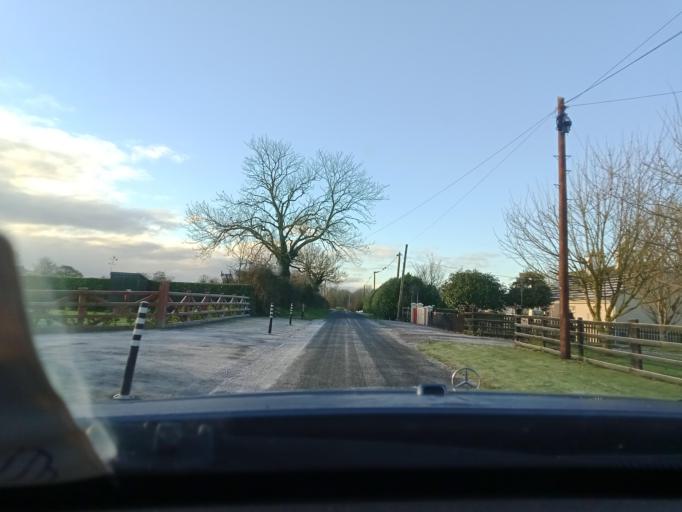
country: IE
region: Leinster
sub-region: County Carlow
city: Bagenalstown
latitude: 52.6474
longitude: -7.0025
